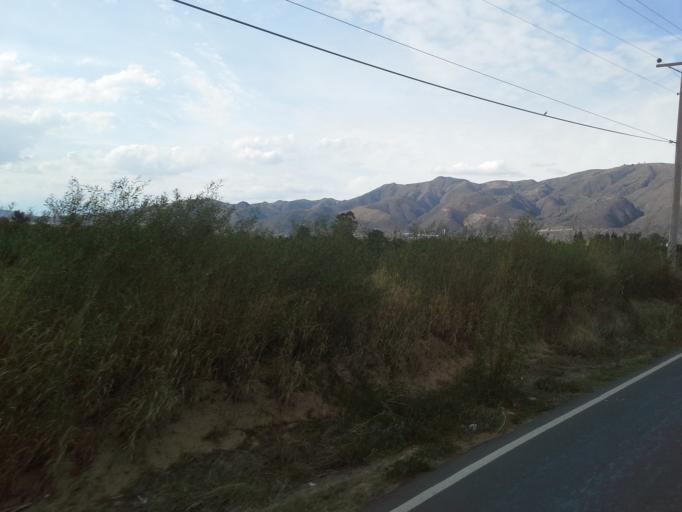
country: BO
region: Cochabamba
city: Tarata
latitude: -17.5699
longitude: -66.0129
